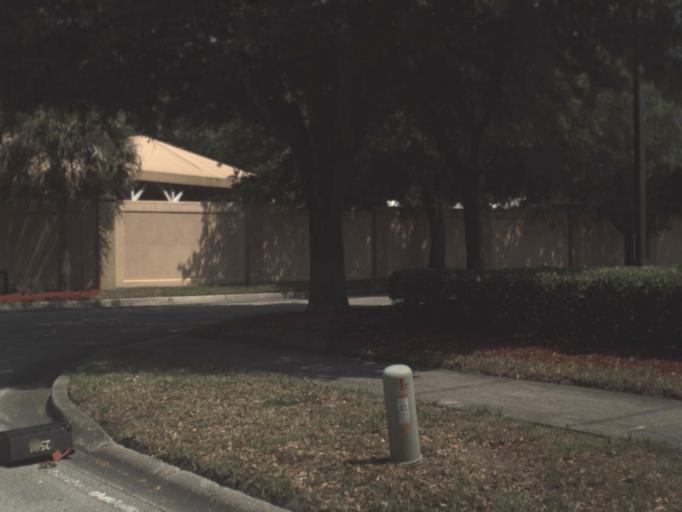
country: US
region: Florida
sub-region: Duval County
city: Atlantic Beach
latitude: 30.3562
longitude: -81.4129
